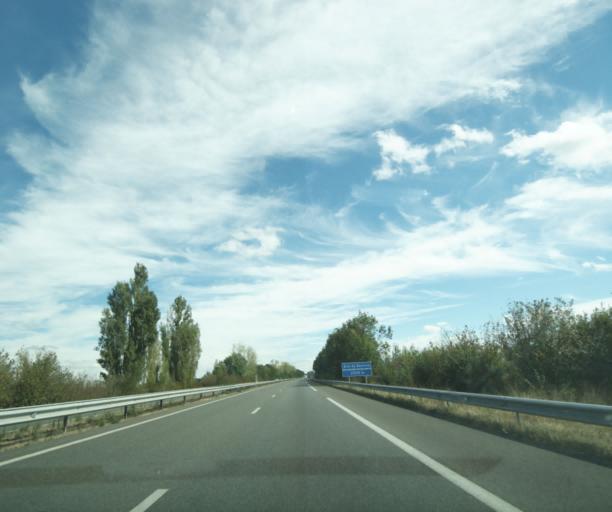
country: FR
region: Midi-Pyrenees
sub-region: Departement du Tarn-et-Garonne
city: Saint-Nicolas-de-la-Grave
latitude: 44.0512
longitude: 0.9755
